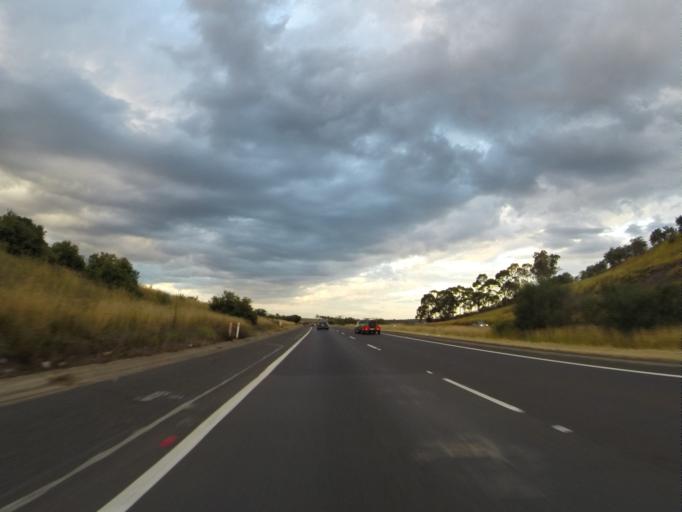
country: AU
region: New South Wales
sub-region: Wollondilly
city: Douglas Park
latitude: -34.1732
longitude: 150.7318
